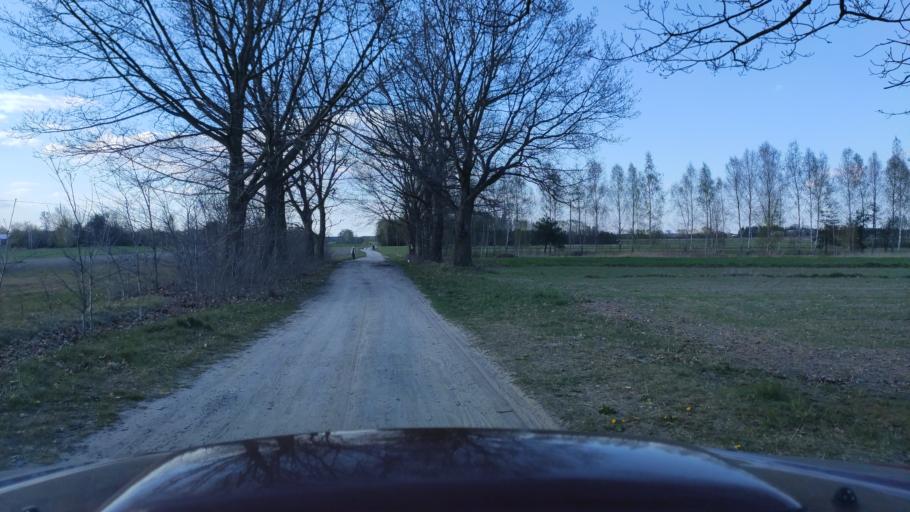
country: PL
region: Masovian Voivodeship
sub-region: Powiat zwolenski
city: Zwolen
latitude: 51.3655
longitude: 21.5756
